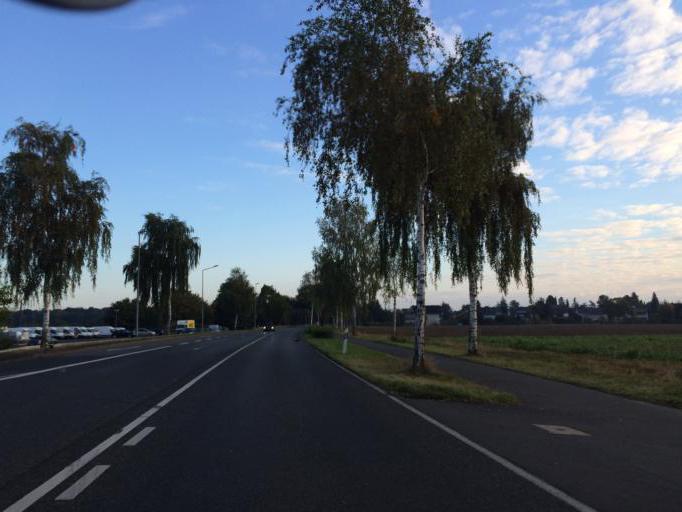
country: DE
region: North Rhine-Westphalia
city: Sankt Augustin
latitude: 50.7657
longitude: 7.1759
